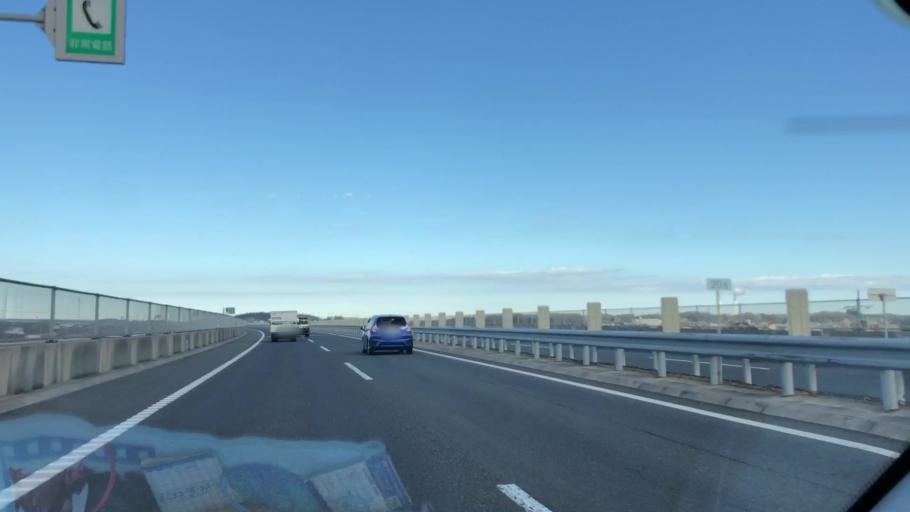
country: JP
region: Chiba
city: Kisarazu
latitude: 35.4023
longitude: 139.9662
